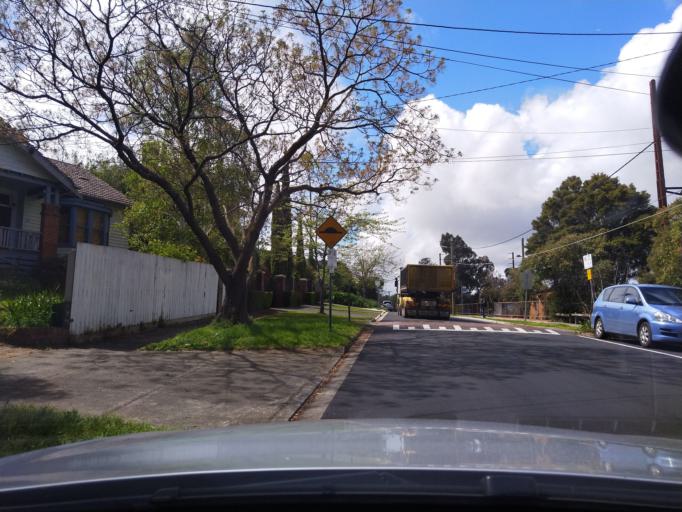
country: AU
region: Victoria
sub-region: Banyule
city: Bellfield
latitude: -37.7640
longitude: 145.0530
